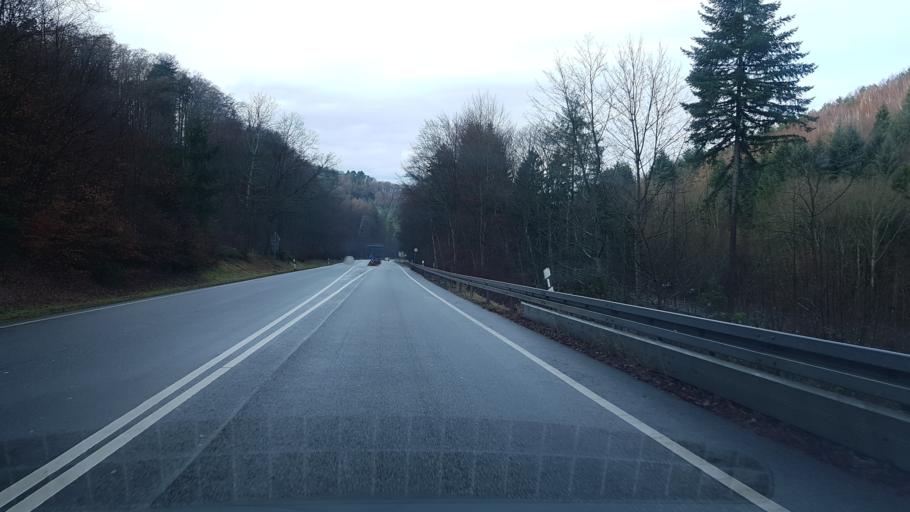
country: DE
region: Saarland
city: Sankt Ingbert
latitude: 49.2556
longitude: 7.1104
